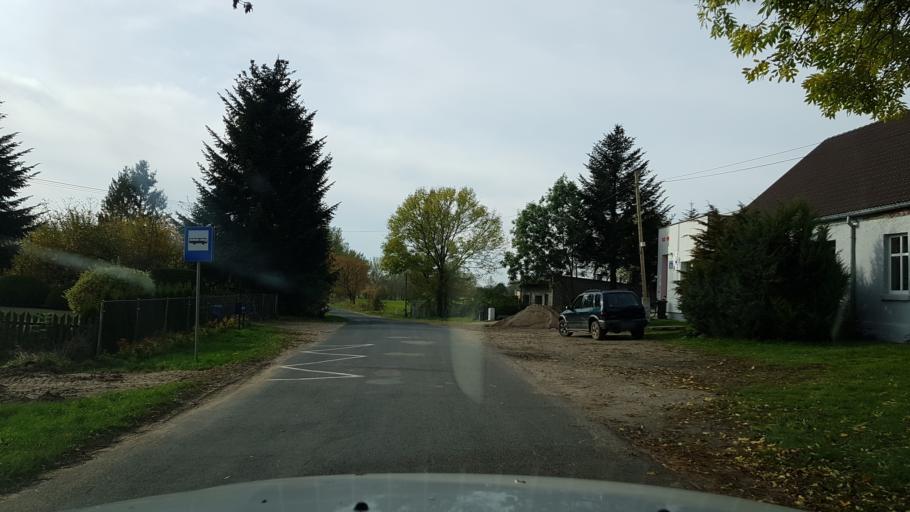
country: PL
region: West Pomeranian Voivodeship
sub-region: Powiat swidwinski
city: Polczyn-Zdroj
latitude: 53.7438
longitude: 16.0367
